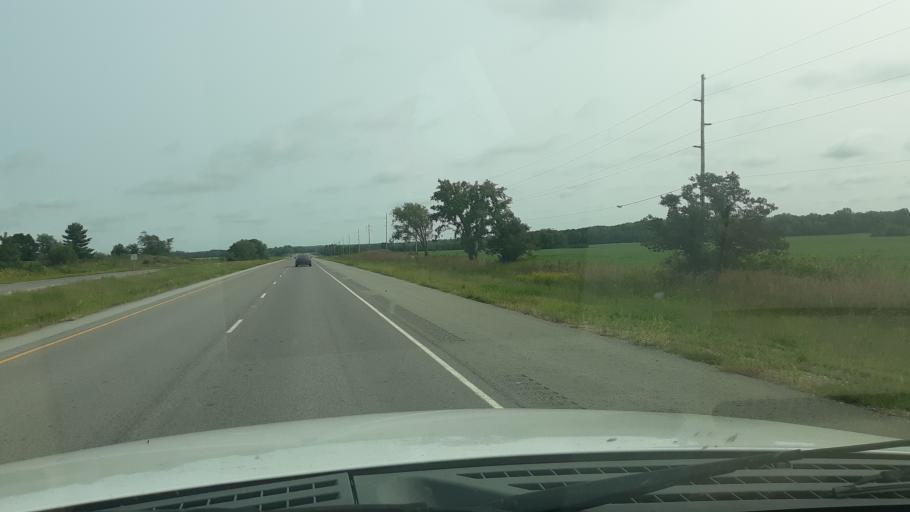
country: US
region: Illinois
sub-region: Saline County
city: Eldorado
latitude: 37.8568
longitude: -88.4059
